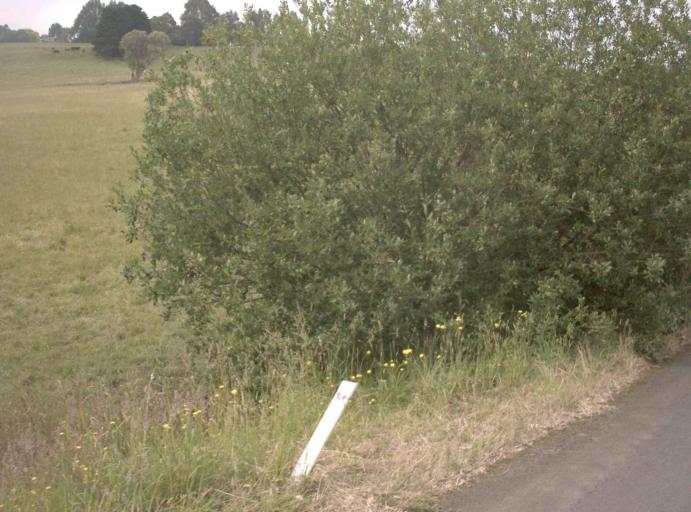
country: AU
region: Victoria
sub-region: Baw Baw
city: Warragul
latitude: -38.4097
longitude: 146.0499
